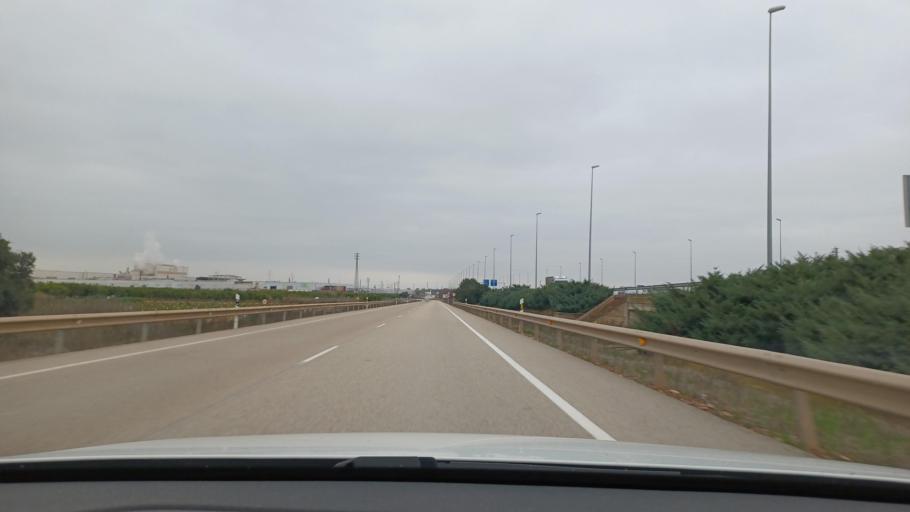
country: ES
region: Valencia
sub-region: Provincia de Castello
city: Villavieja
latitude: 39.8482
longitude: -0.1753
